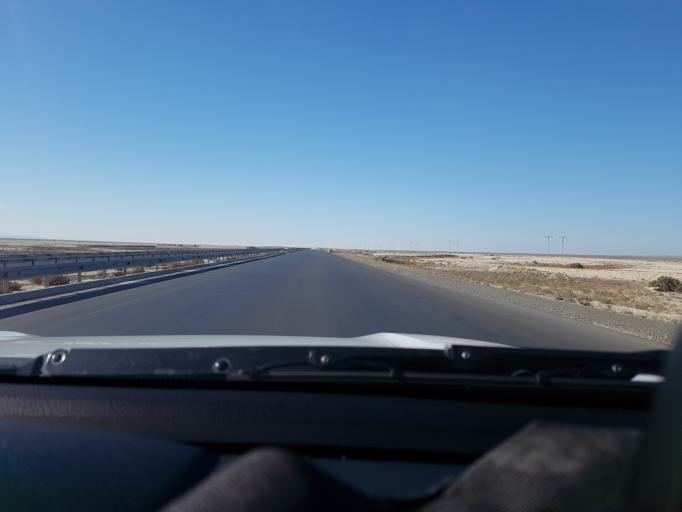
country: TM
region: Balkan
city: Gazanjyk
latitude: 39.2617
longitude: 55.1142
